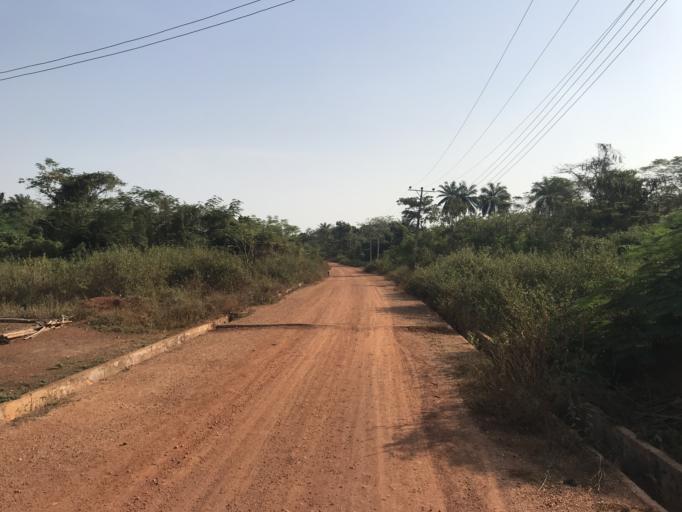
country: NG
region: Osun
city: Bode Osi
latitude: 7.7718
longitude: 4.3044
